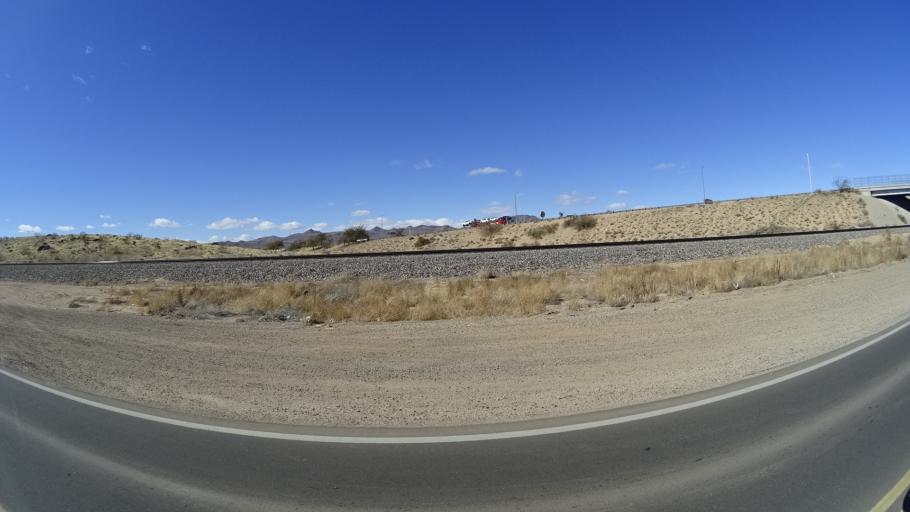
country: US
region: Arizona
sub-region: Mohave County
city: Kingman
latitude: 35.2158
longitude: -114.0078
